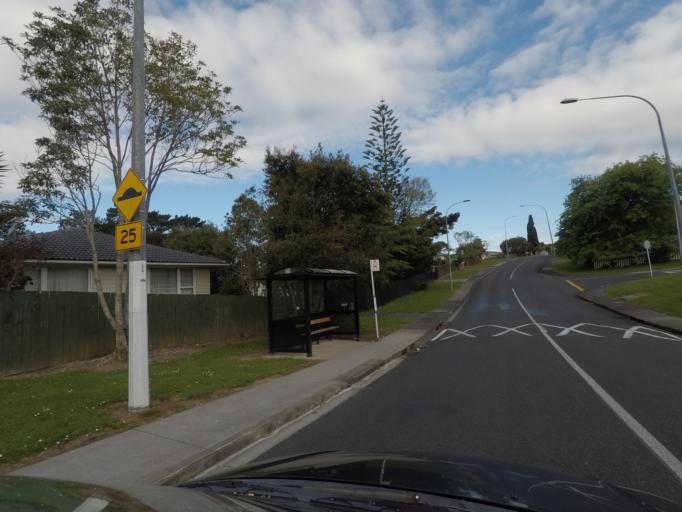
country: NZ
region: Auckland
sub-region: Auckland
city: Rosebank
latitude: -36.8872
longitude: 174.6510
